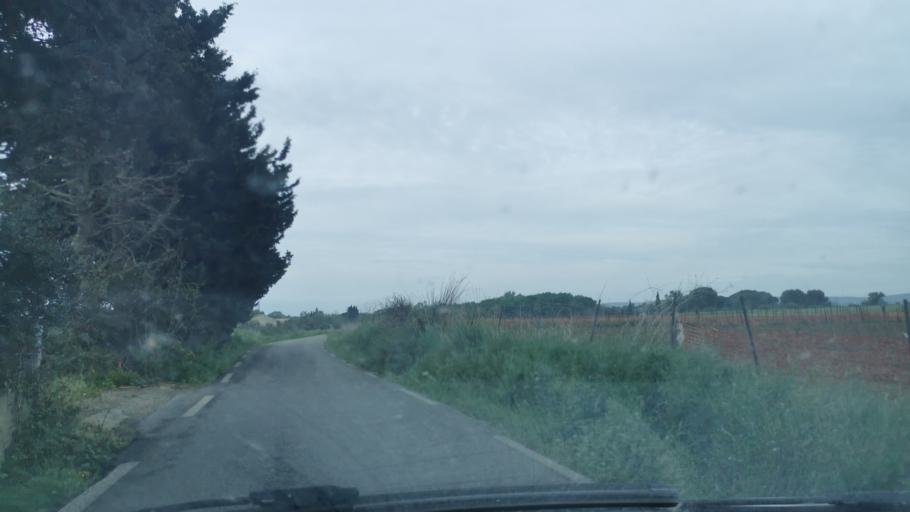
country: FR
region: Languedoc-Roussillon
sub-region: Departement de l'Herault
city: Fabregues
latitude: 43.5607
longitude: 3.7703
